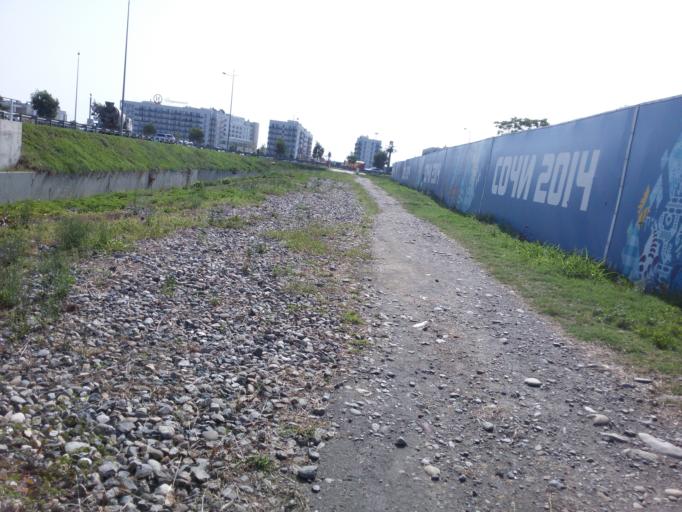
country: RU
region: Krasnodarskiy
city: Adler
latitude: 43.4151
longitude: 39.9382
